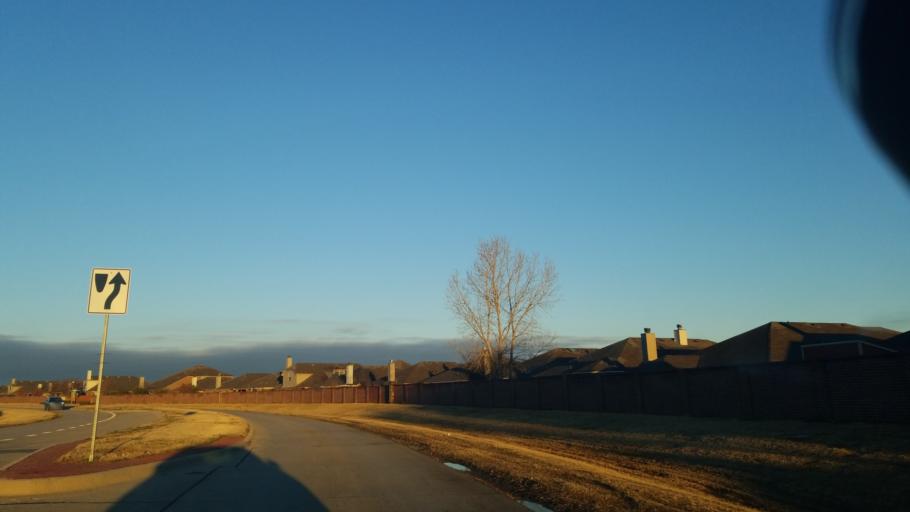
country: US
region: Texas
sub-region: Denton County
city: Denton
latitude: 33.1694
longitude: -97.1605
